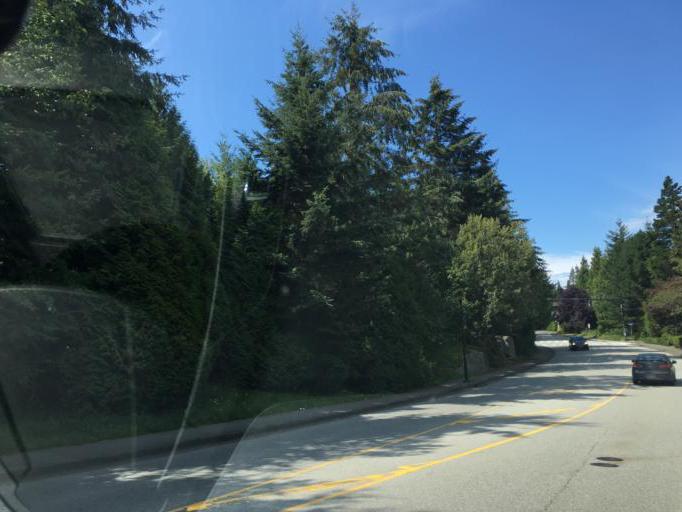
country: CA
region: British Columbia
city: West Vancouver
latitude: 49.3505
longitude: -123.2529
